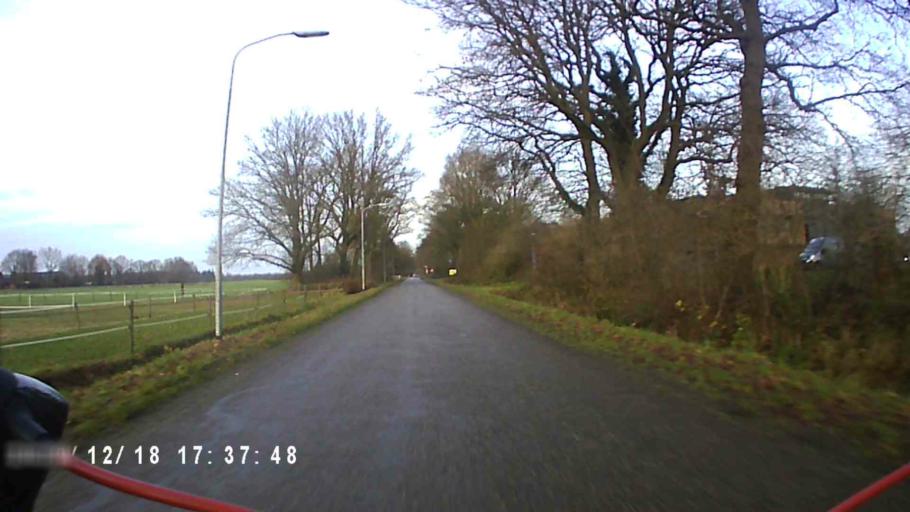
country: NL
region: Drenthe
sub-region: Gemeente Tynaarlo
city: Vries
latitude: 53.0857
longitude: 6.5763
